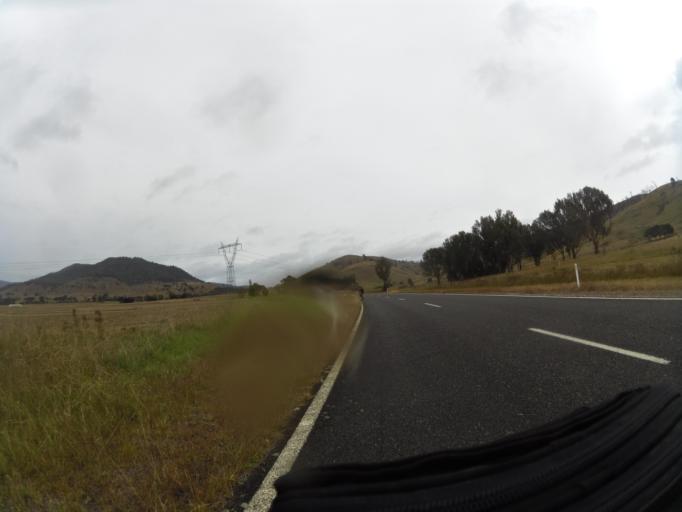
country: AU
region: New South Wales
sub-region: Greater Hume Shire
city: Holbrook
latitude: -36.2083
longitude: 147.7351
